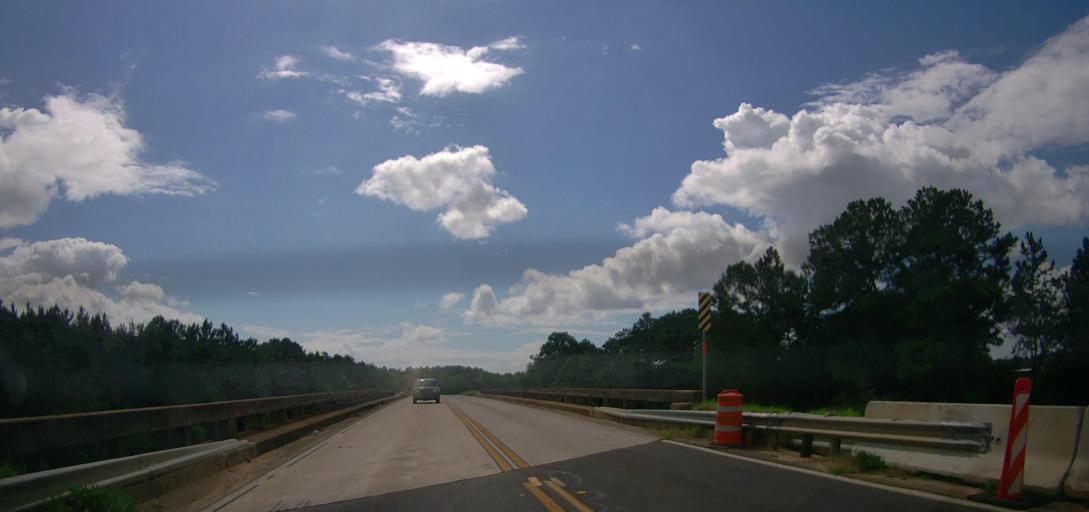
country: US
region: Georgia
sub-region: Coffee County
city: Broxton
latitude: 31.5475
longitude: -82.9405
